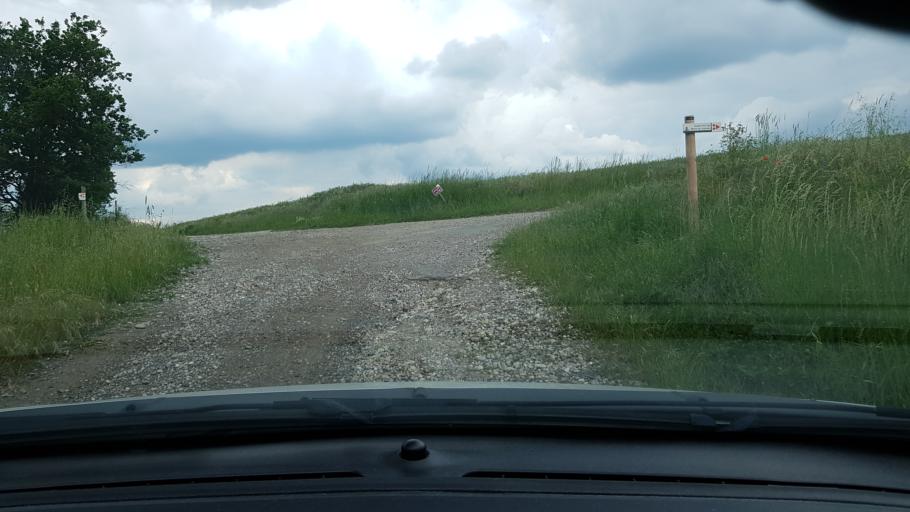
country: FR
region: Rhone-Alpes
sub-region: Departement du Rhone
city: Chassagny
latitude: 45.6092
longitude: 4.7124
